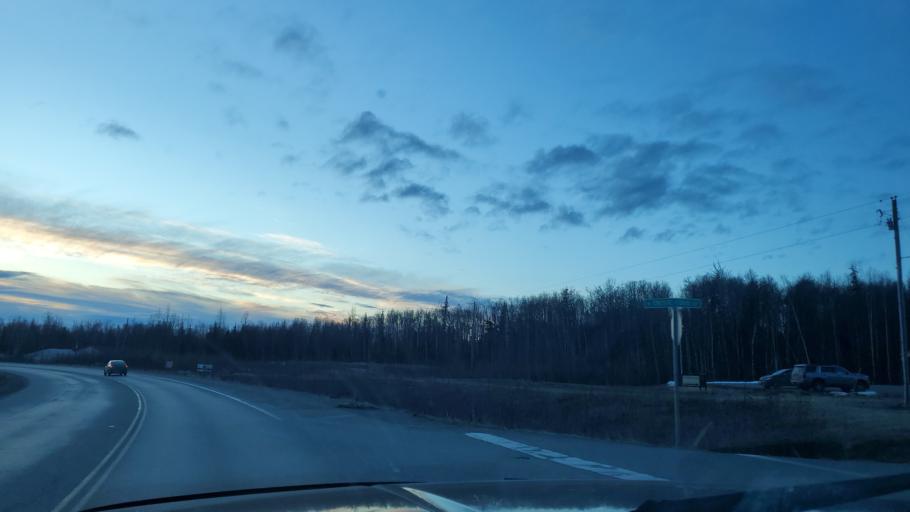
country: US
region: Alaska
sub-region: Matanuska-Susitna Borough
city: Wasilla
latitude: 61.5939
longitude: -149.4364
